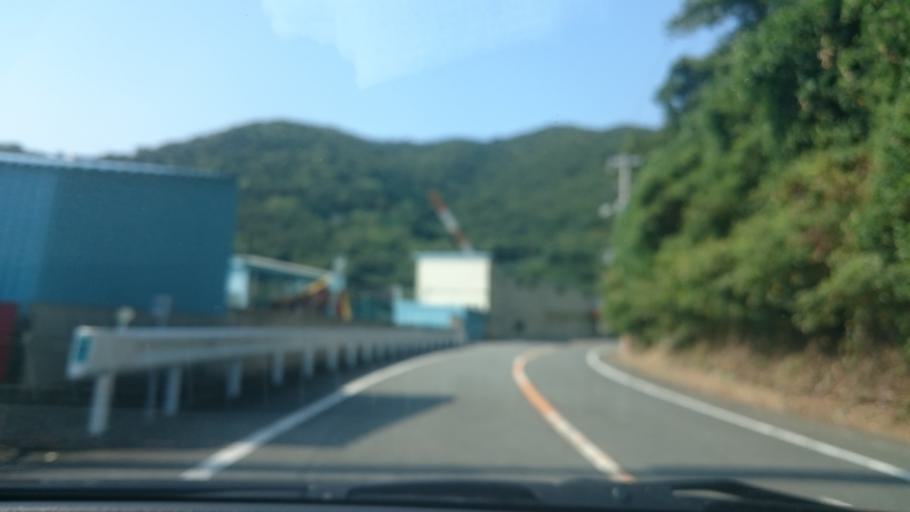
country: JP
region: Shizuoka
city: Heda
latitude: 34.9768
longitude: 138.7757
